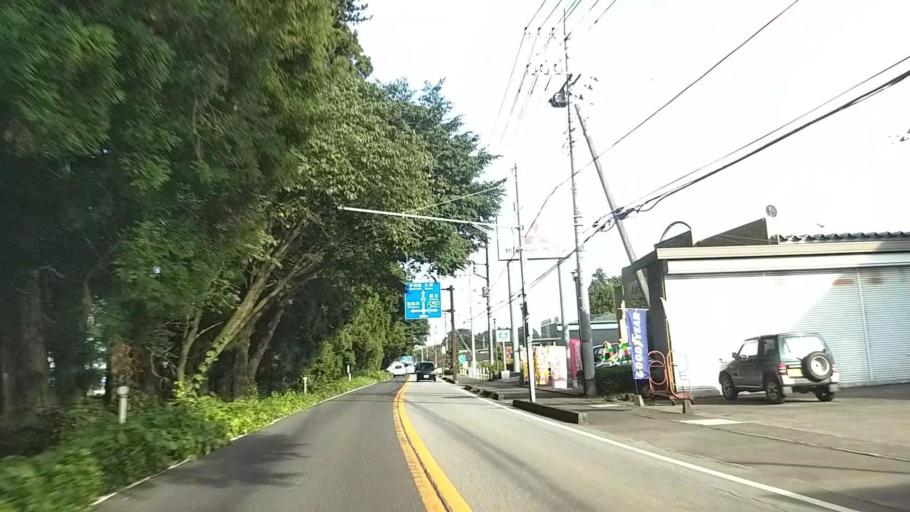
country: JP
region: Tochigi
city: Imaichi
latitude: 36.7175
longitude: 139.7153
